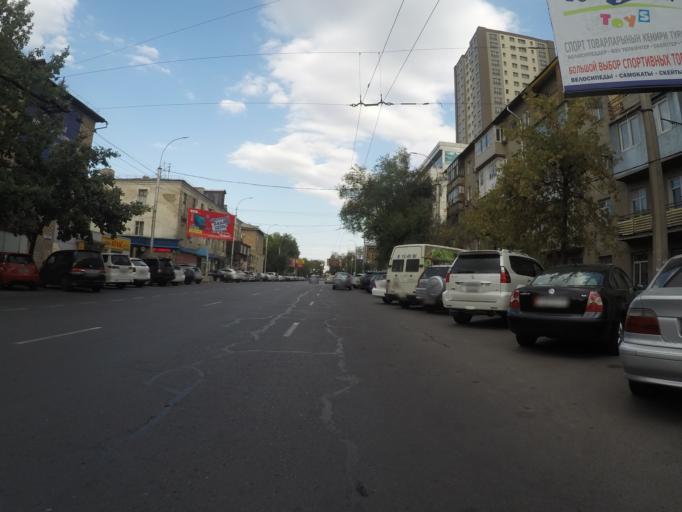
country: KG
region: Chuy
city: Bishkek
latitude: 42.8753
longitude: 74.5892
